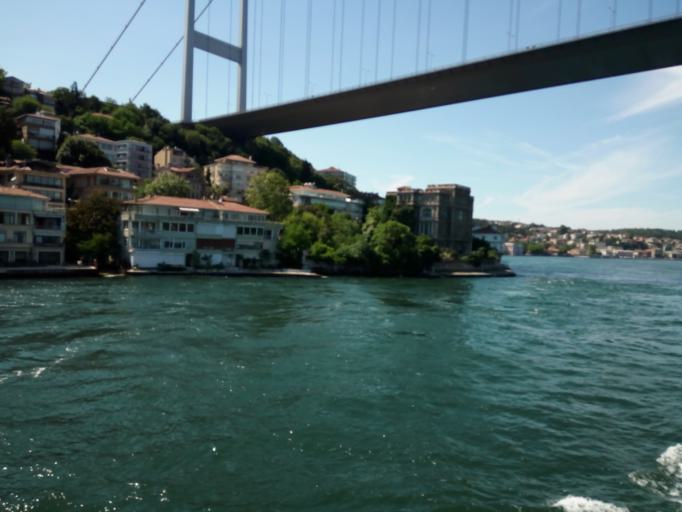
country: TR
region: Istanbul
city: UEskuedar
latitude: 41.0895
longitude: 29.0580
